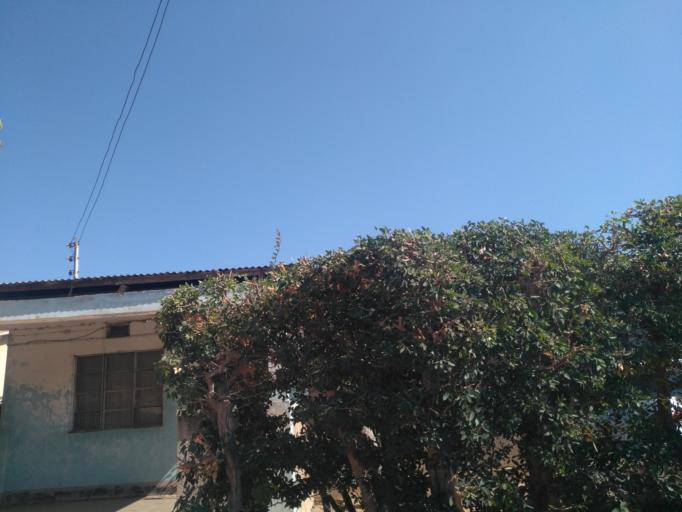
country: TZ
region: Dodoma
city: Dodoma
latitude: -6.1595
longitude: 35.7509
